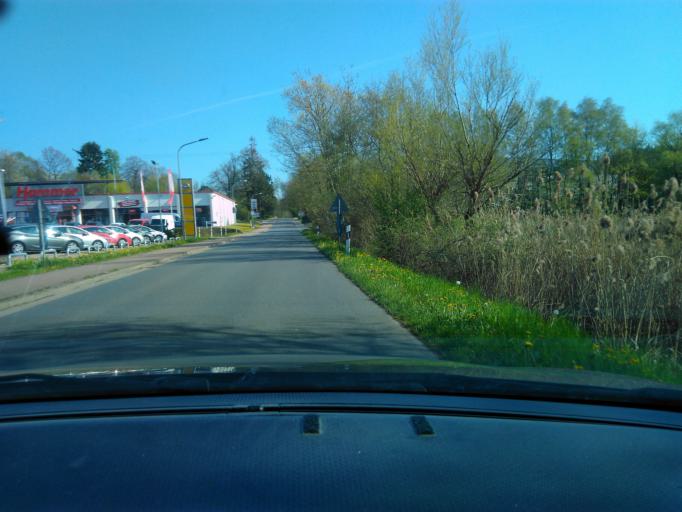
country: DE
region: Lower Saxony
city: Osterode am Harz
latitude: 51.7156
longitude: 10.2738
